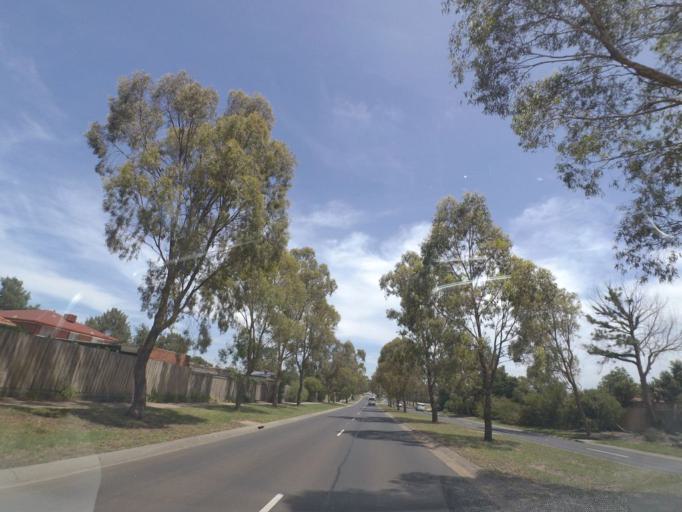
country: AU
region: Victoria
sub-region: Hume
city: Roxburgh Park
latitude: -37.6319
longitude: 144.9235
